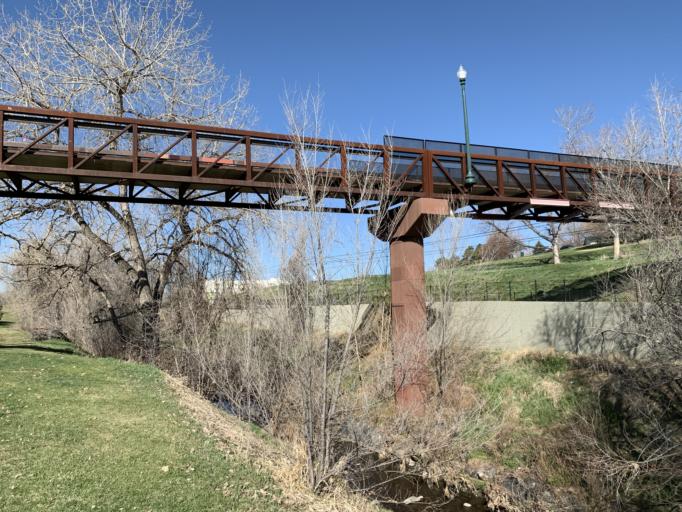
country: US
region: Colorado
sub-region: Jefferson County
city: Edgewater
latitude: 39.7358
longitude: -105.0277
